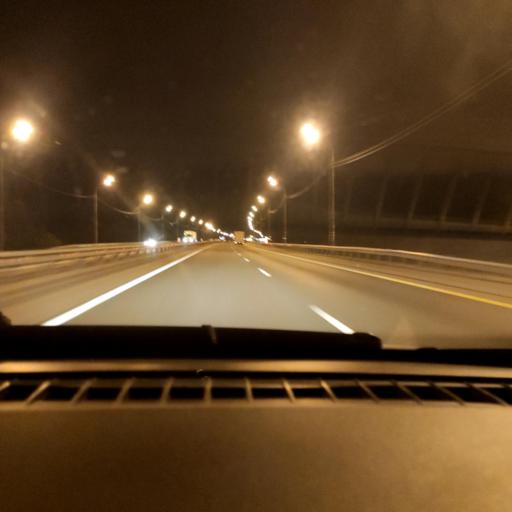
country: RU
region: Lipetsk
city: Khlevnoye
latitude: 52.1347
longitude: 39.1993
